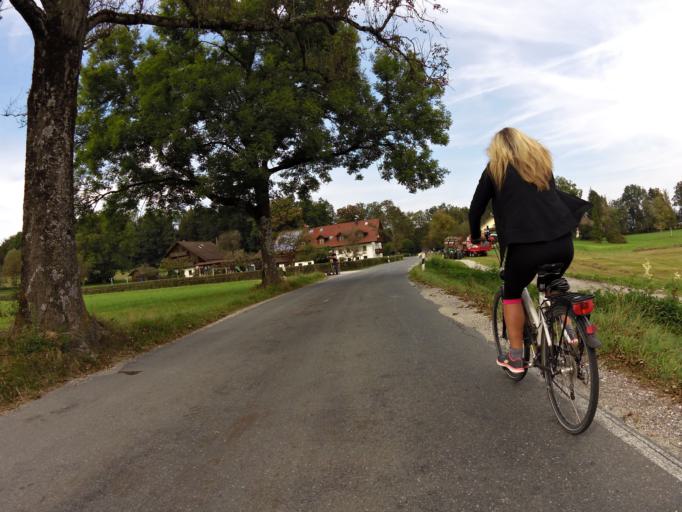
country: DE
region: Bavaria
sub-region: Upper Bavaria
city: Seeshaupt
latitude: 47.8339
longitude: 11.2881
